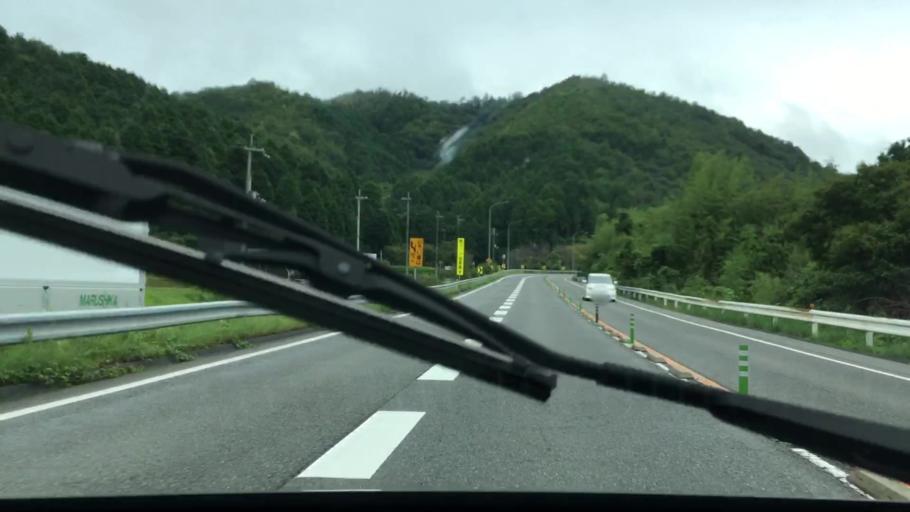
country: JP
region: Hyogo
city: Himeji
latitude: 35.0028
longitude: 134.7671
